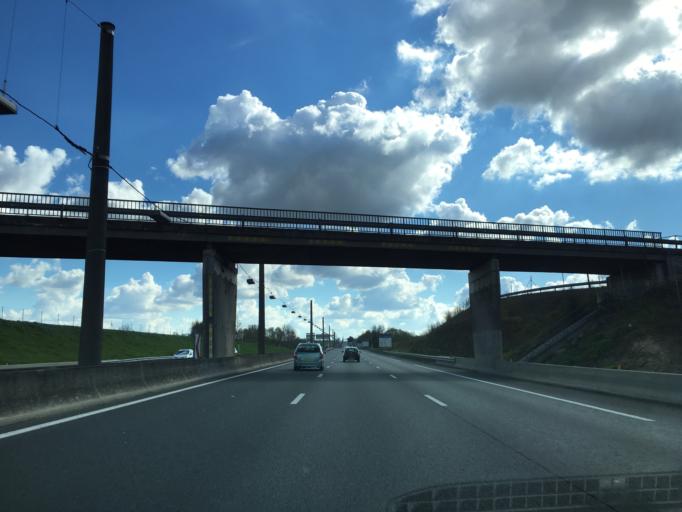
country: FR
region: Nord-Pas-de-Calais
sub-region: Departement du Pas-de-Calais
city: Roeux
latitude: 50.2998
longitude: 2.8874
